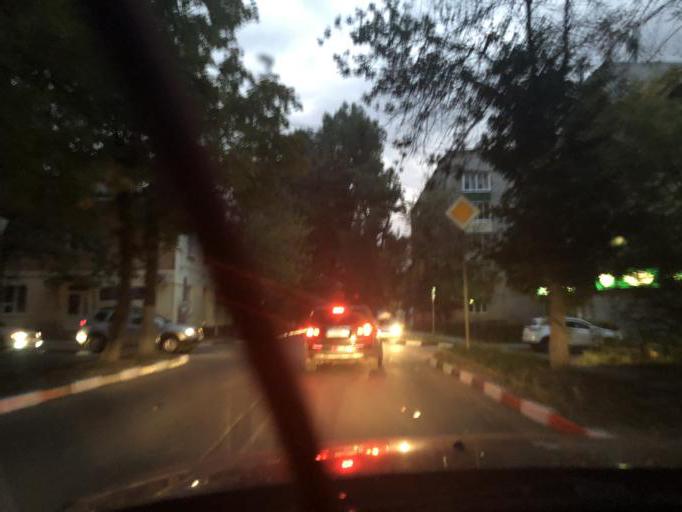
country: RU
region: Tula
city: Gorelki
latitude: 54.2267
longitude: 37.6178
